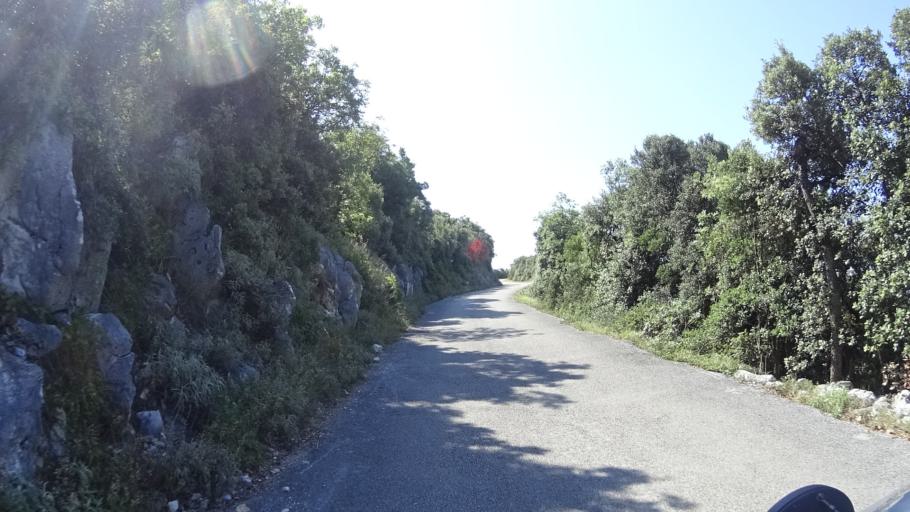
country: HR
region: Istarska
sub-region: Grad Labin
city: Rabac
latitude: 44.9701
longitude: 14.1446
